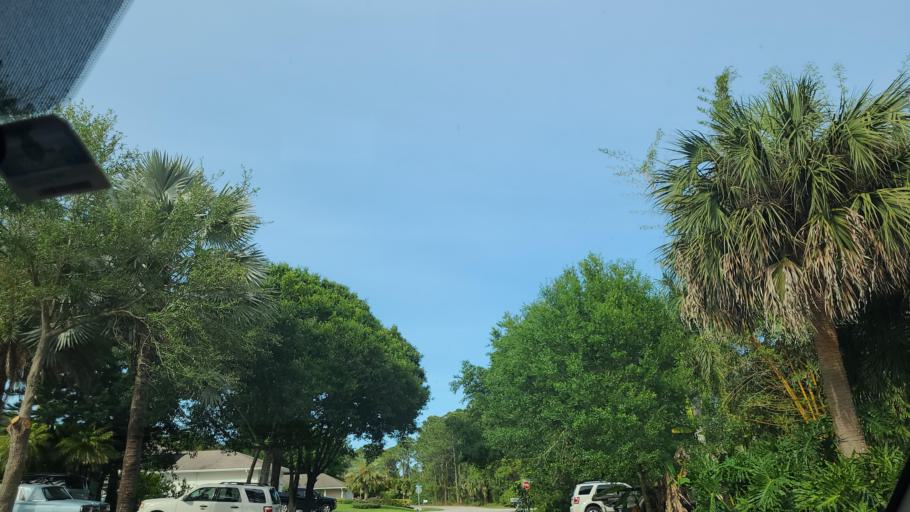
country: US
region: Florida
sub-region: Indian River County
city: Sebastian
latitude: 27.7881
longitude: -80.4876
